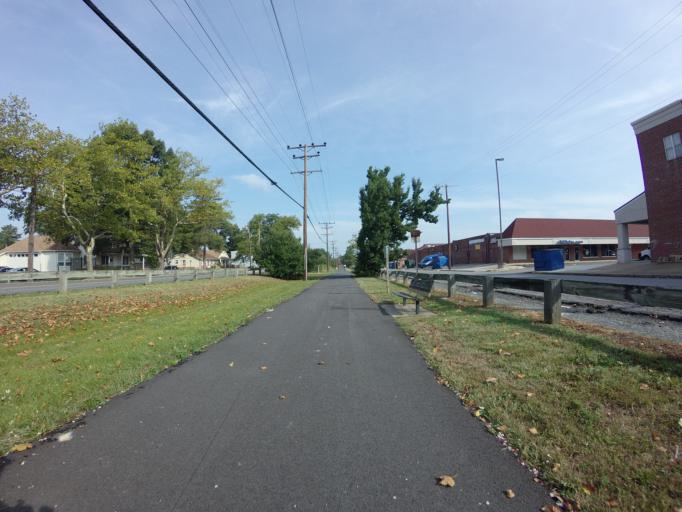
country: US
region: Maryland
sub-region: Anne Arundel County
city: Glen Burnie
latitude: 39.1586
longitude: -76.6211
